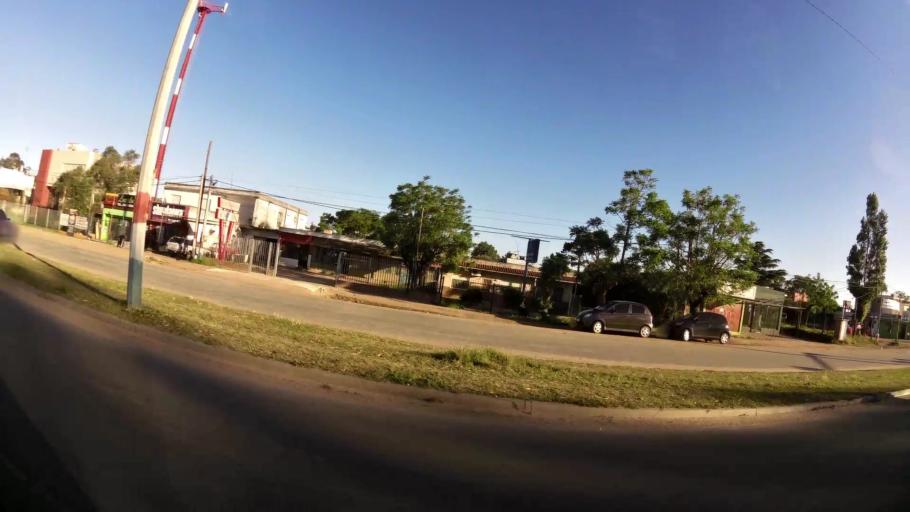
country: UY
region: Canelones
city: Paso de Carrasco
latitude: -34.8606
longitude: -56.0516
